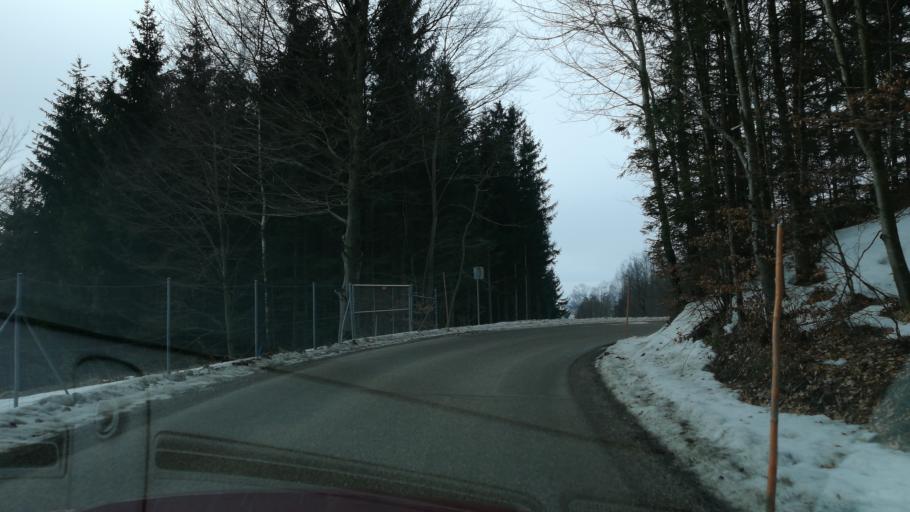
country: AT
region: Upper Austria
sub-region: Politischer Bezirk Vocklabruck
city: Zell am Pettenfirst
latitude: 48.1457
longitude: 13.6009
